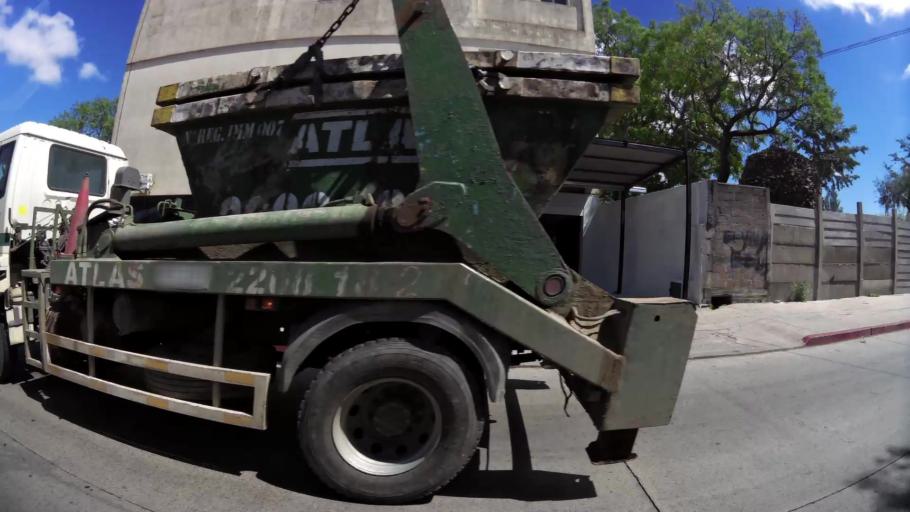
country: UY
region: Montevideo
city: Montevideo
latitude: -34.8539
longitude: -56.1398
